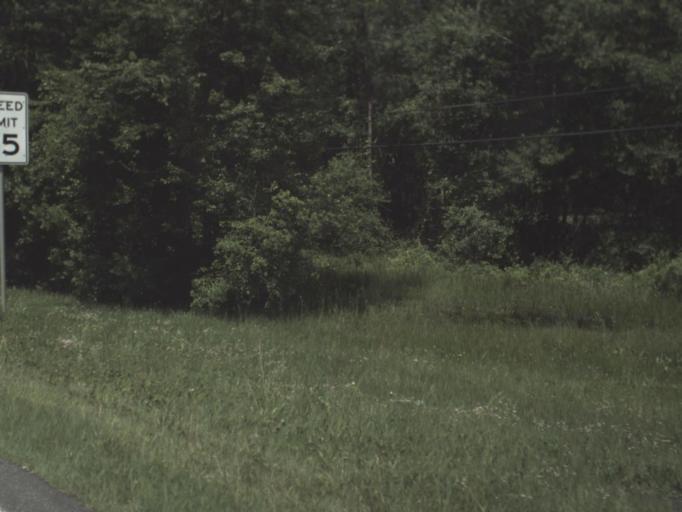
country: US
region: Florida
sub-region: Duval County
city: Baldwin
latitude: 30.3123
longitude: -81.9695
